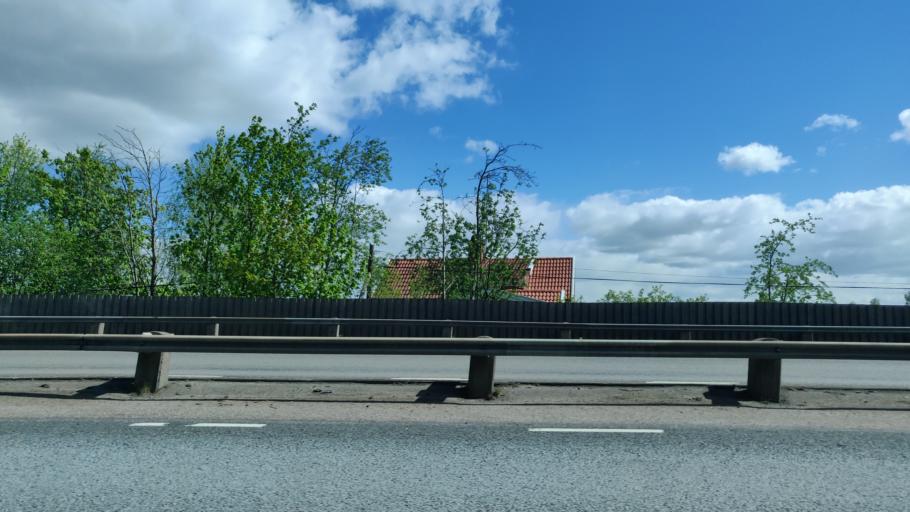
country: SE
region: Vaermland
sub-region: Karlstads Kommun
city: Karlstad
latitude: 59.3951
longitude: 13.5347
